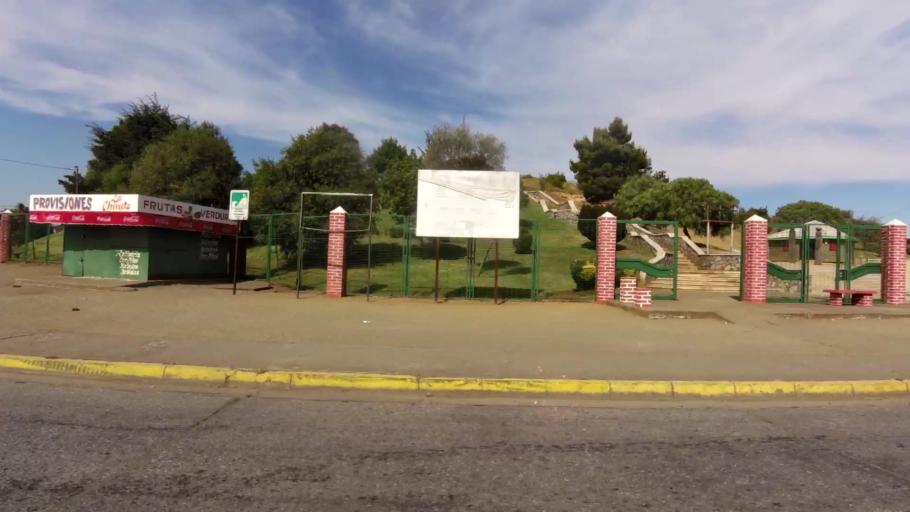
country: CL
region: Biobio
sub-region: Provincia de Concepcion
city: Talcahuano
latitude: -36.7835
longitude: -73.1017
